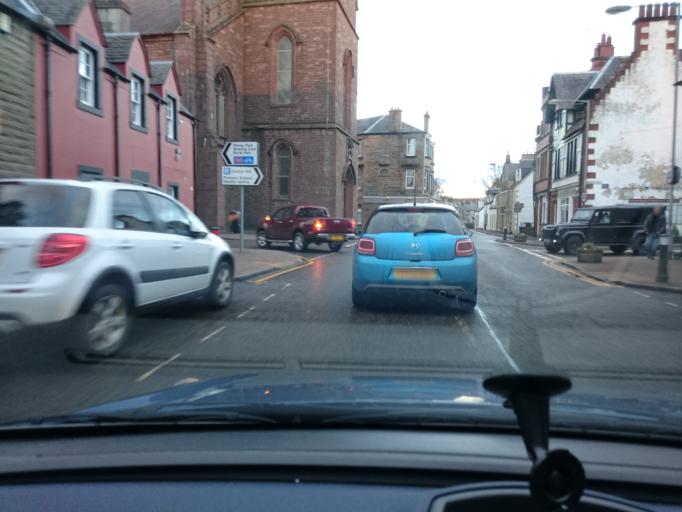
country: GB
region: Scotland
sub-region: Stirling
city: Doune
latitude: 56.1893
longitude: -4.0510
